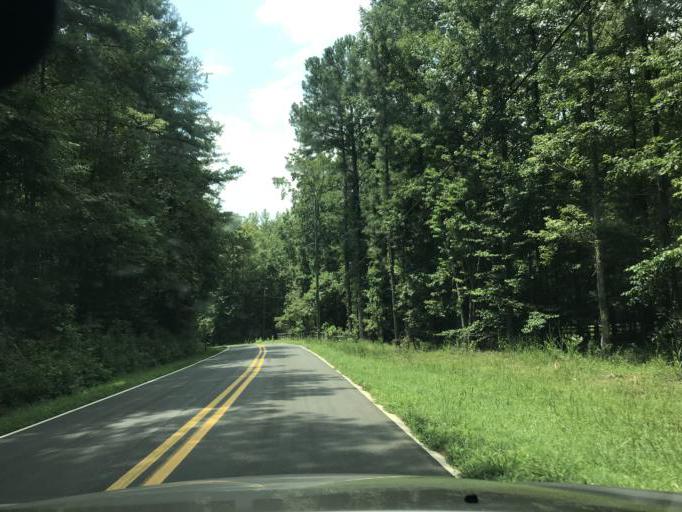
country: US
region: Georgia
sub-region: Dawson County
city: Dawsonville
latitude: 34.3289
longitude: -84.2113
